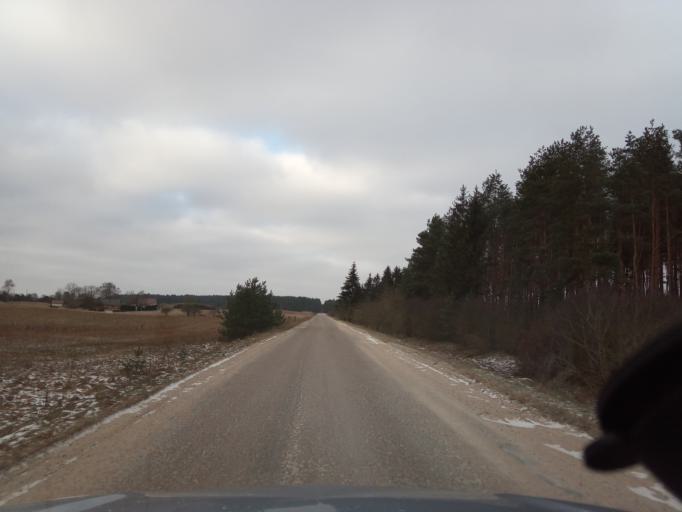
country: LT
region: Alytaus apskritis
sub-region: Alytaus rajonas
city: Daugai
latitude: 54.3292
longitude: 24.2965
